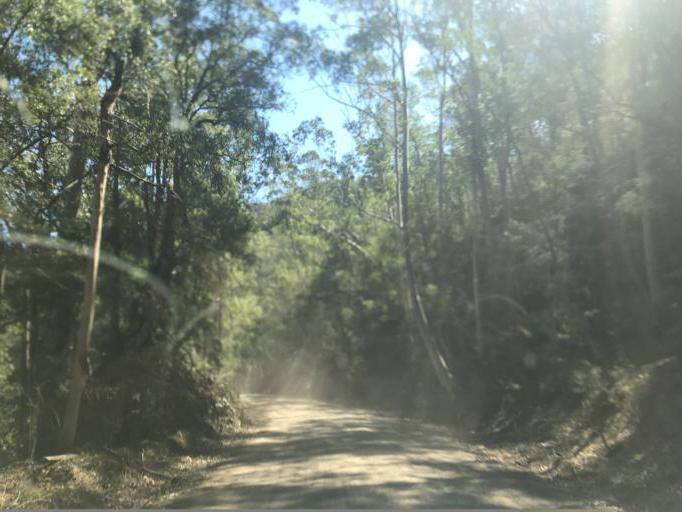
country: AU
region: New South Wales
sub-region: Wyong Shire
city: Little Jilliby
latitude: -33.1973
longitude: 151.0216
